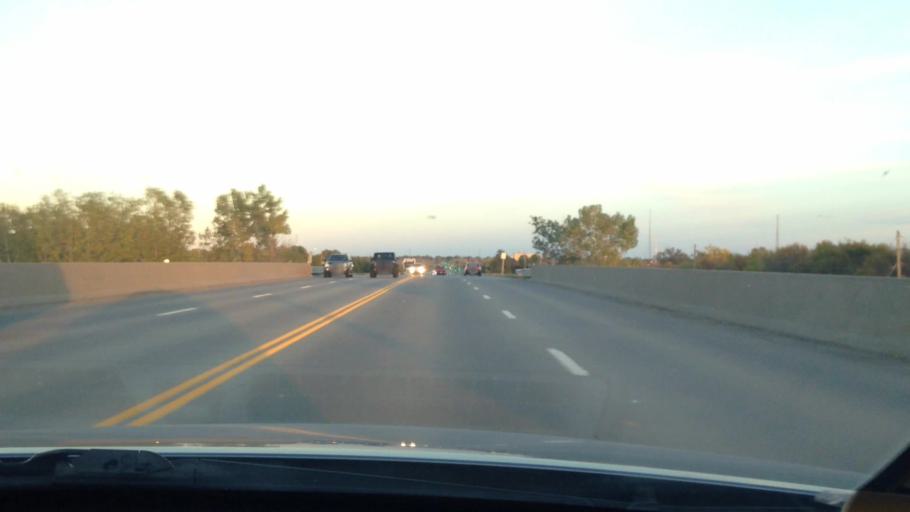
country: US
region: Kansas
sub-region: Johnson County
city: Olathe
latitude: 38.8677
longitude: -94.8240
